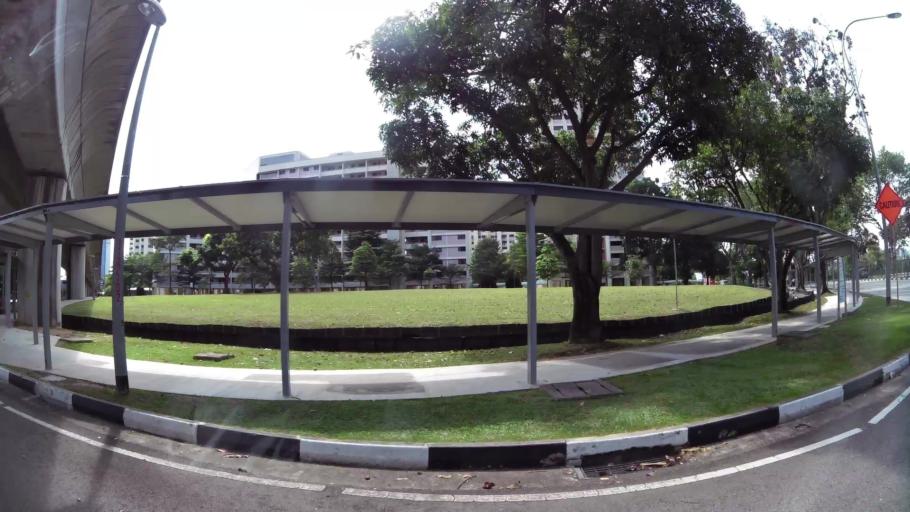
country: SG
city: Singapore
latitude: 1.3407
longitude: 103.7348
